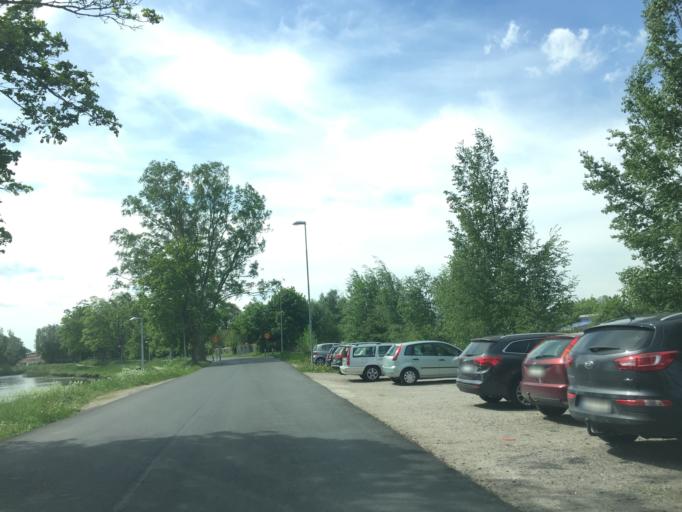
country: SE
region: OErebro
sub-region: Orebro Kommun
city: Orebro
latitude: 59.2746
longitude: 15.2468
